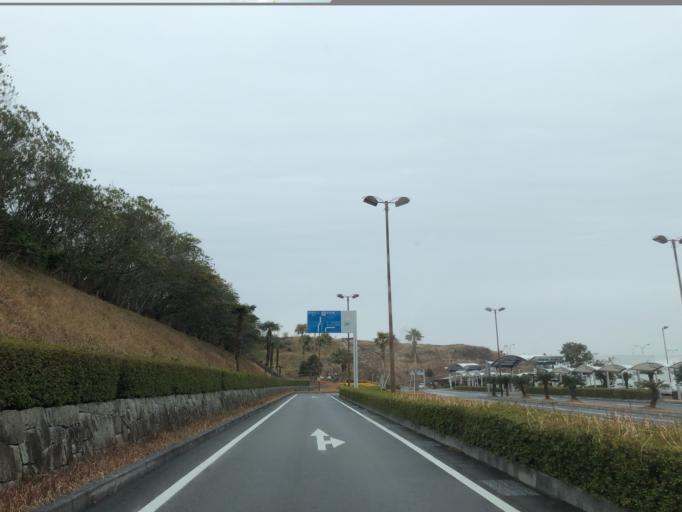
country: JP
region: Wakayama
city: Tanabe
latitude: 33.6620
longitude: 135.3600
